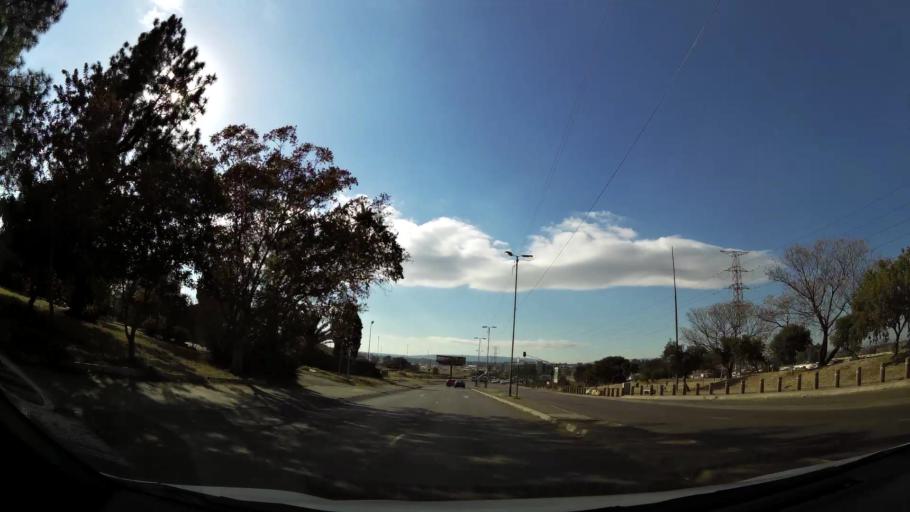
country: ZA
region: Gauteng
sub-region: City of Tshwane Metropolitan Municipality
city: Pretoria
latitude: -25.7182
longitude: 28.3541
